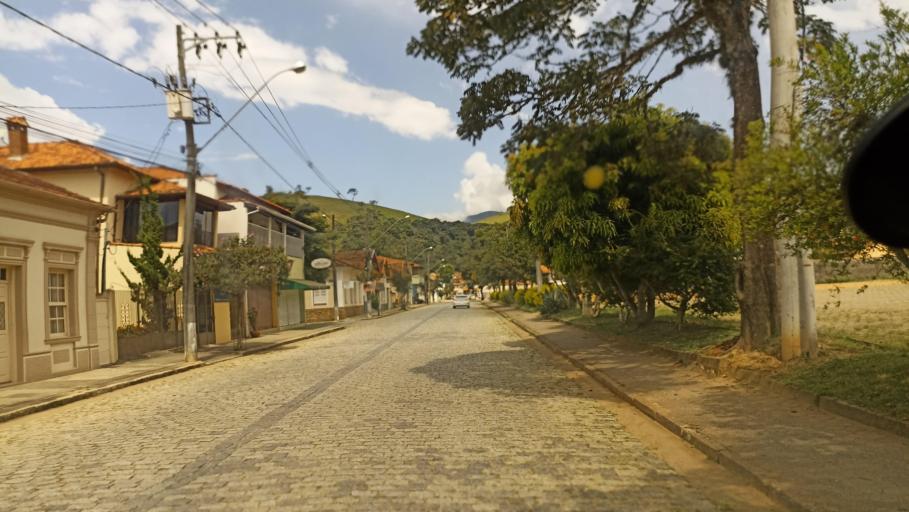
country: BR
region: Minas Gerais
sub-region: Passa Quatro
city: Passa Quatro
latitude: -22.3900
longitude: -44.9650
